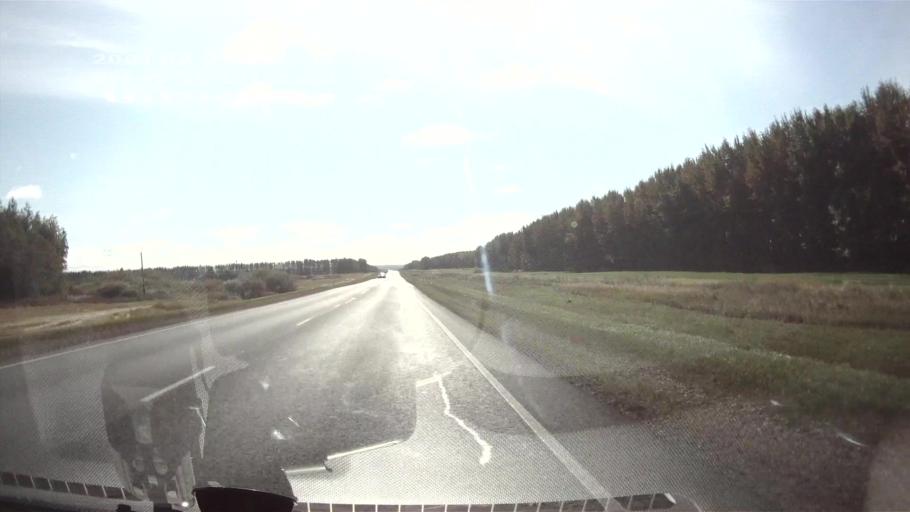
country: RU
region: Ulyanovsk
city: Tsil'na
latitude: 54.5570
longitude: 47.9320
